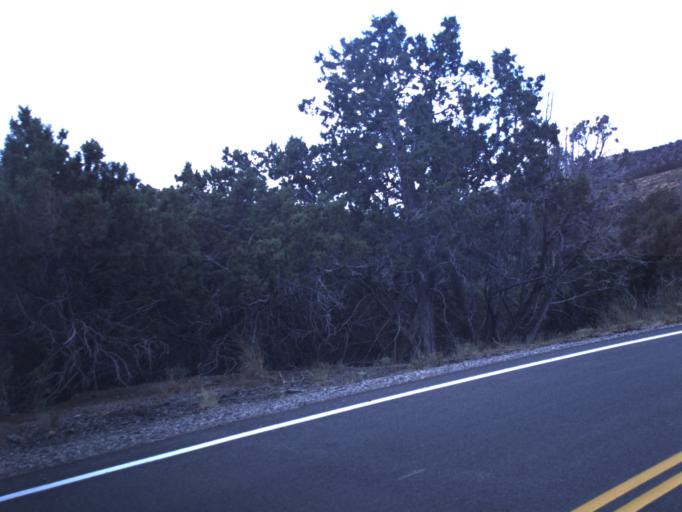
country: US
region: Utah
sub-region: Tooele County
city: Grantsville
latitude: 40.3445
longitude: -112.5651
